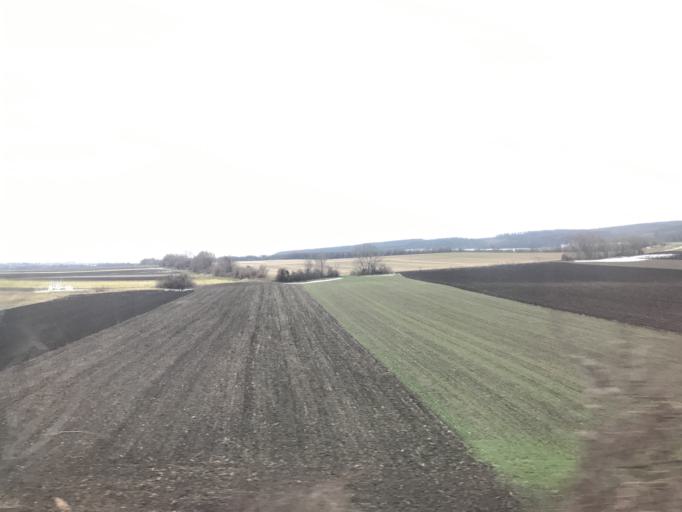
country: AT
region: Burgenland
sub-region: Politischer Bezirk Neusiedl am See
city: Parndorf
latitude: 47.9978
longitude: 16.8372
